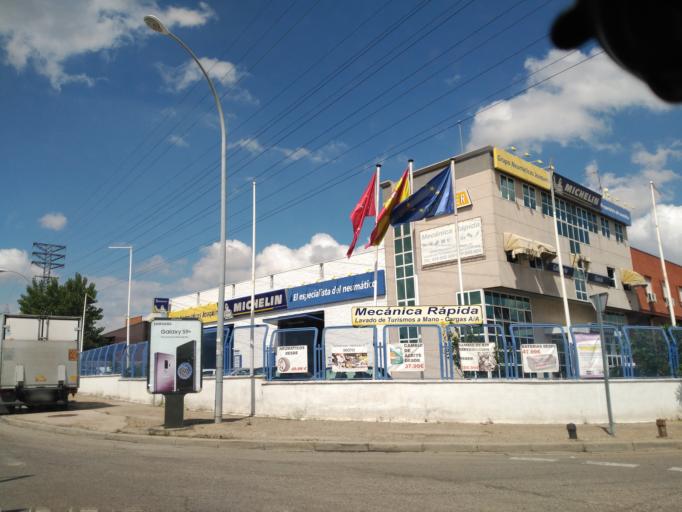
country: ES
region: Madrid
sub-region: Provincia de Madrid
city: Getafe
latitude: 40.3020
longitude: -3.7029
